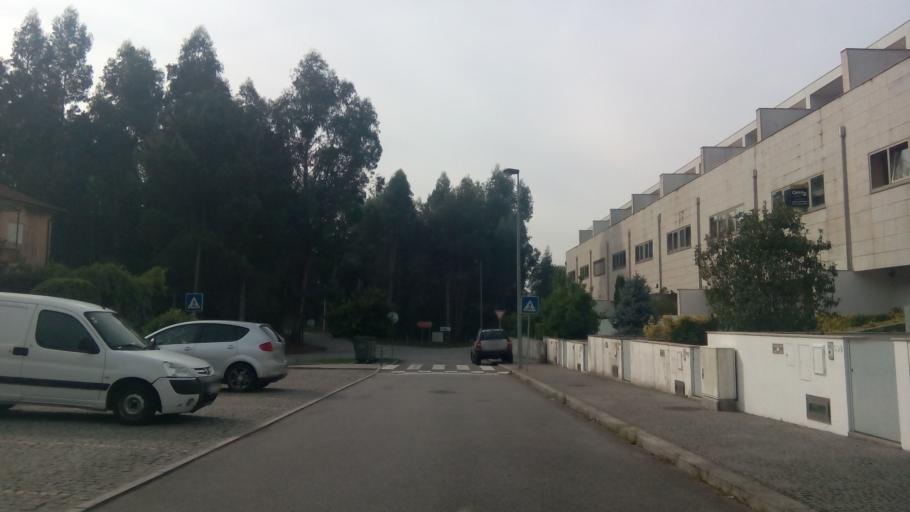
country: PT
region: Porto
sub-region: Paredes
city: Gandra
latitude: 41.1882
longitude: -8.4252
